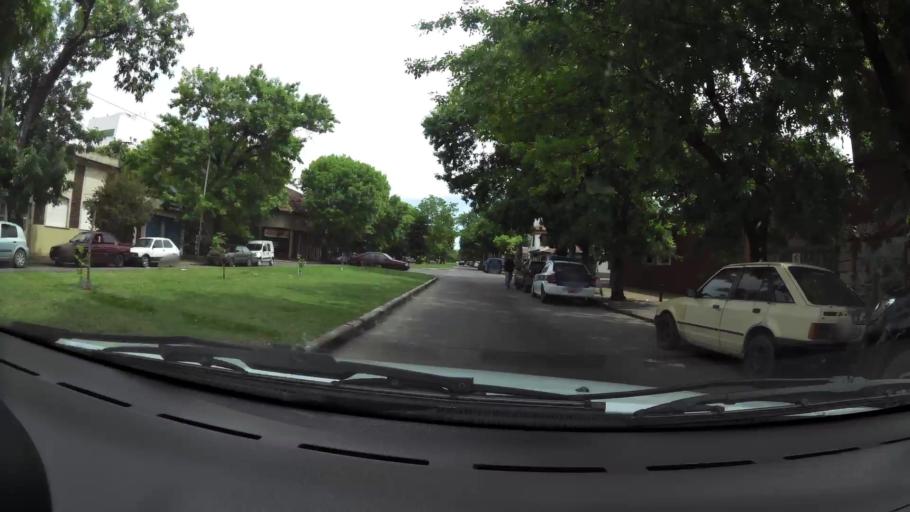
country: AR
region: Buenos Aires
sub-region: Partido de La Plata
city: La Plata
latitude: -34.9333
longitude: -57.9428
